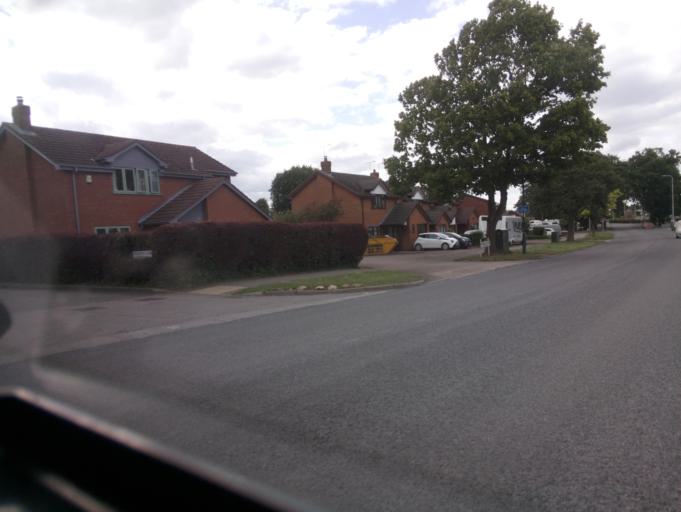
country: GB
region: England
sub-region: Warwickshire
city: Nuneaton
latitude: 52.5384
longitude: -1.4658
